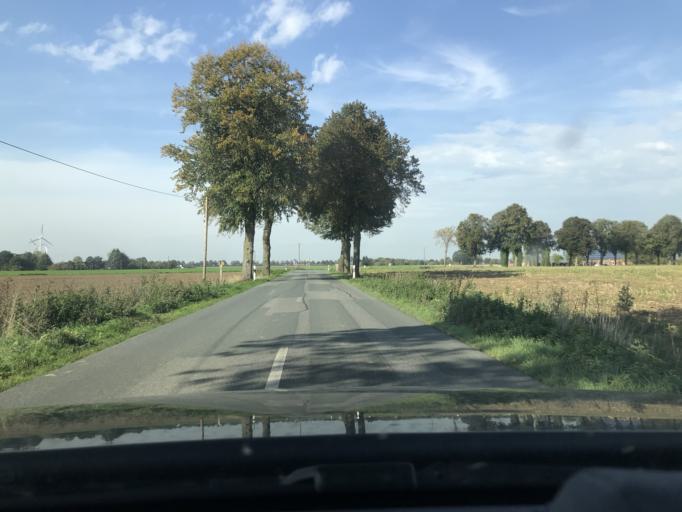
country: DE
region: North Rhine-Westphalia
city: Kalkar
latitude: 51.7006
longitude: 6.2651
